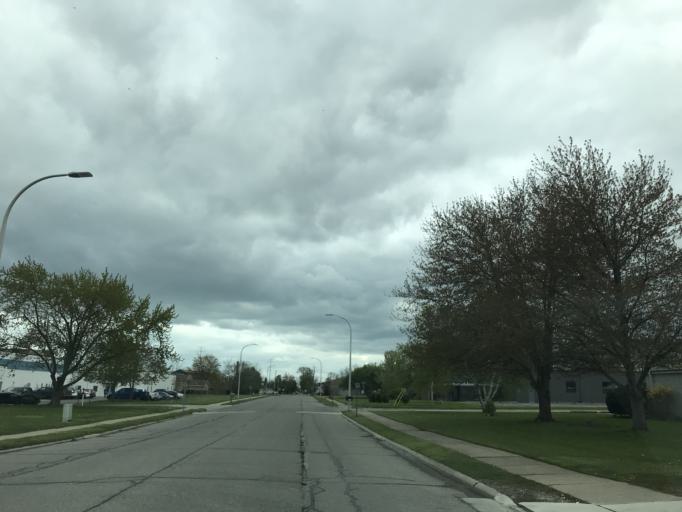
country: US
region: Michigan
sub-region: Wayne County
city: Riverview
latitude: 42.1731
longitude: -83.1742
